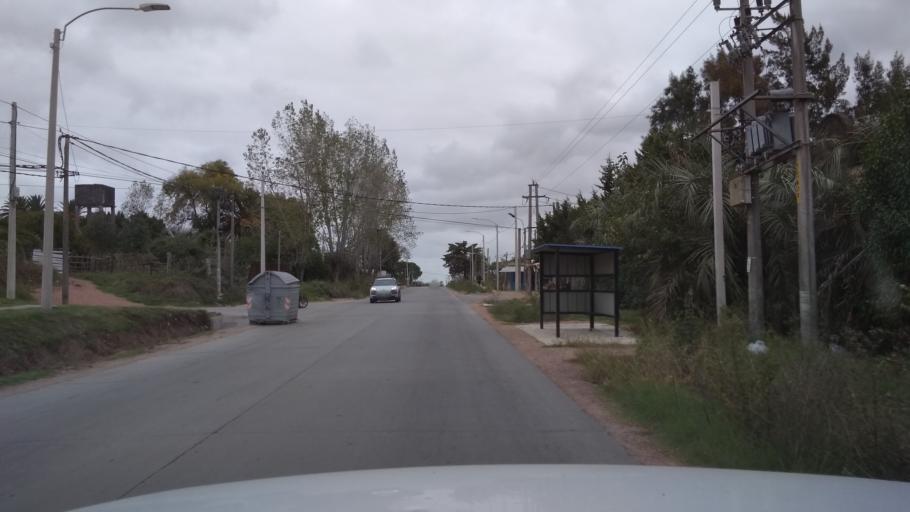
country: UY
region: Canelones
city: Toledo
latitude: -34.7865
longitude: -56.1419
